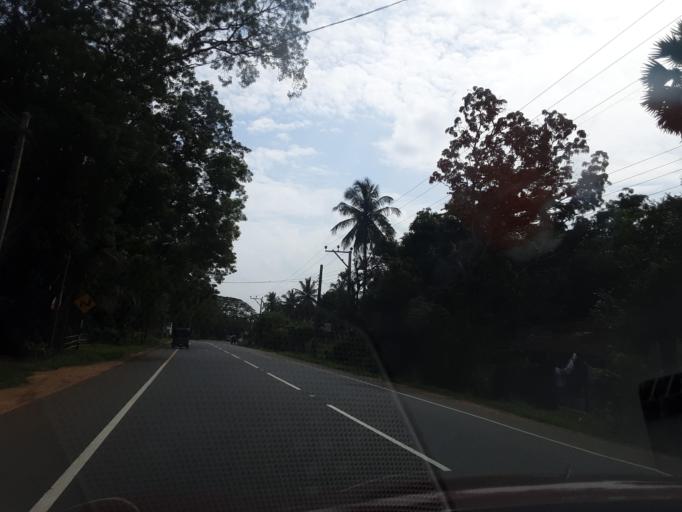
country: LK
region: North Central
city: Anuradhapura
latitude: 8.5200
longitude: 80.5019
